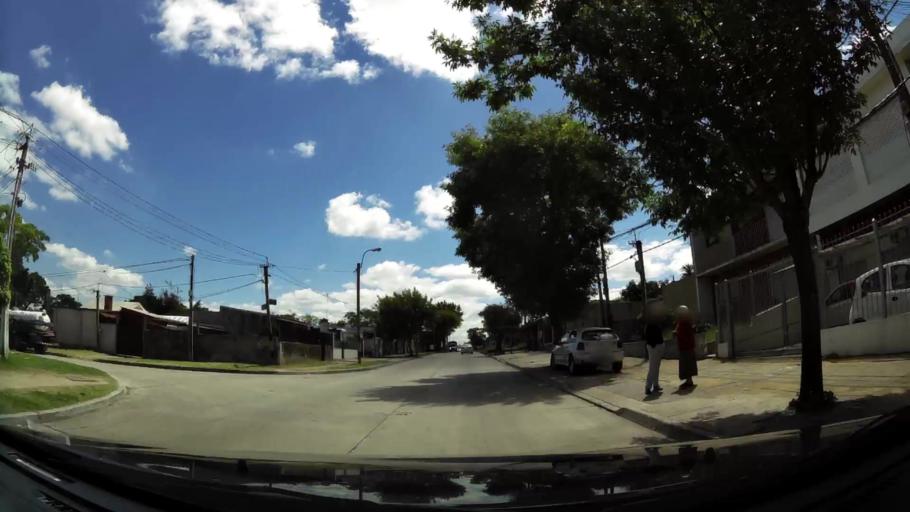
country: UY
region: Montevideo
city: Montevideo
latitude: -34.8498
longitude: -56.1351
